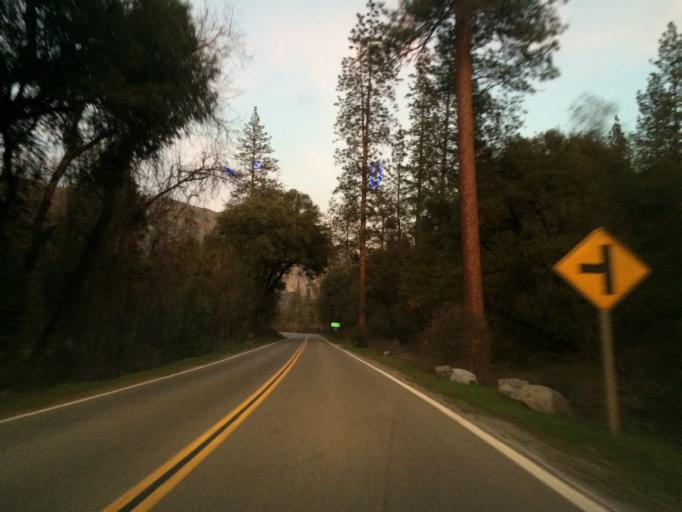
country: US
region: California
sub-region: Mariposa County
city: Midpines
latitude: 37.6726
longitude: -119.7877
